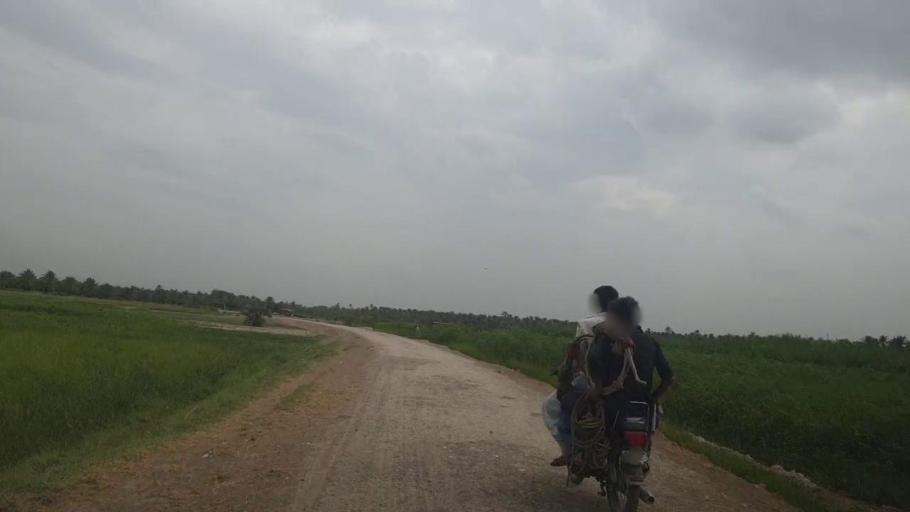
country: PK
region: Sindh
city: Khairpur
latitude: 27.5882
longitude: 68.7400
